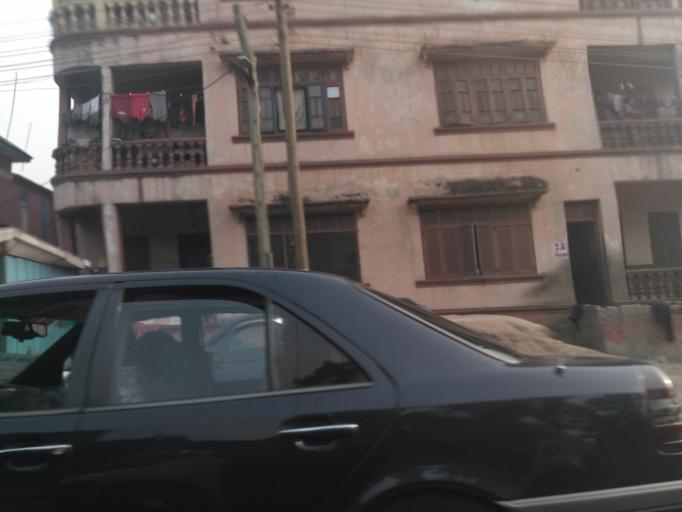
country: GH
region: Ashanti
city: Tafo
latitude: 6.7123
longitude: -1.6211
